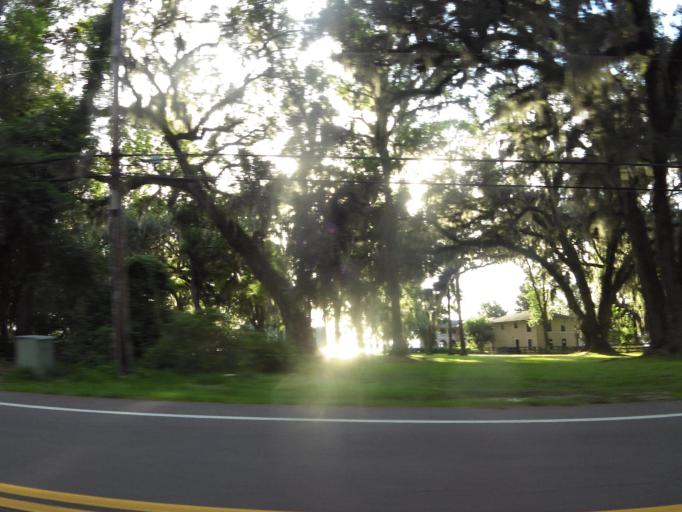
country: US
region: Florida
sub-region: Saint Johns County
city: Fruit Cove
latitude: 30.0590
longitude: -81.6677
